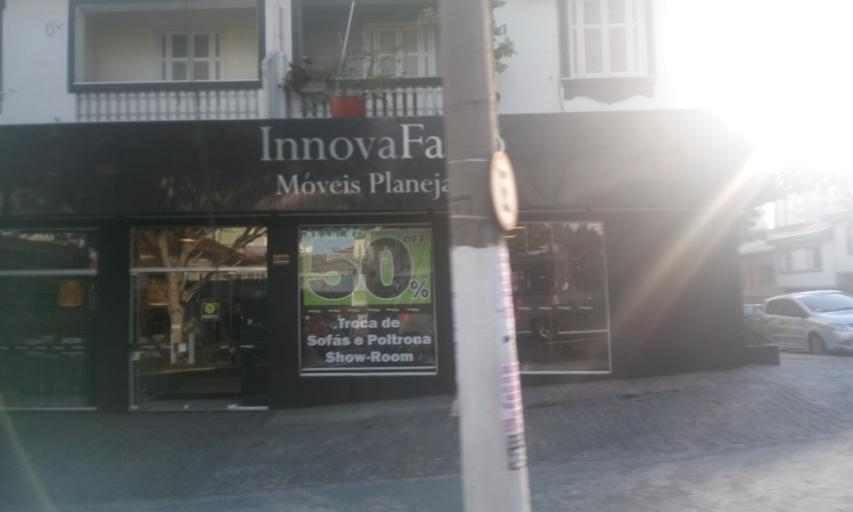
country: BR
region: Sao Paulo
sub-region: Sao Paulo
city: Sao Paulo
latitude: -23.6013
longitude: -46.6095
